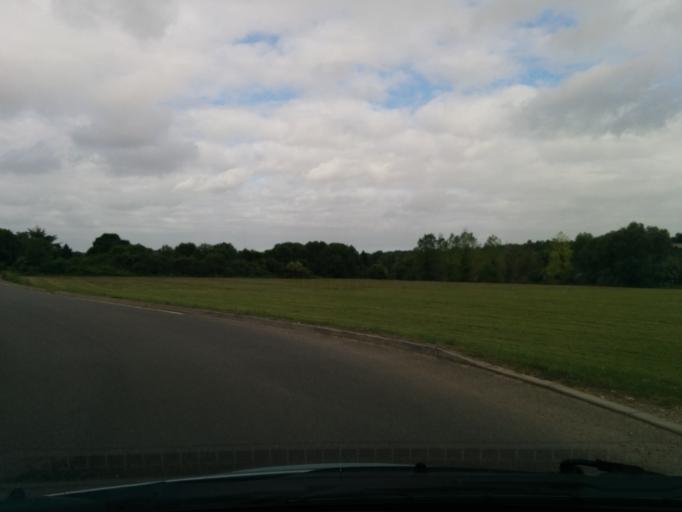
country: FR
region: Ile-de-France
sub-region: Departement des Yvelines
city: Rosny-sur-Seine
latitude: 49.0373
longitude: 1.6520
